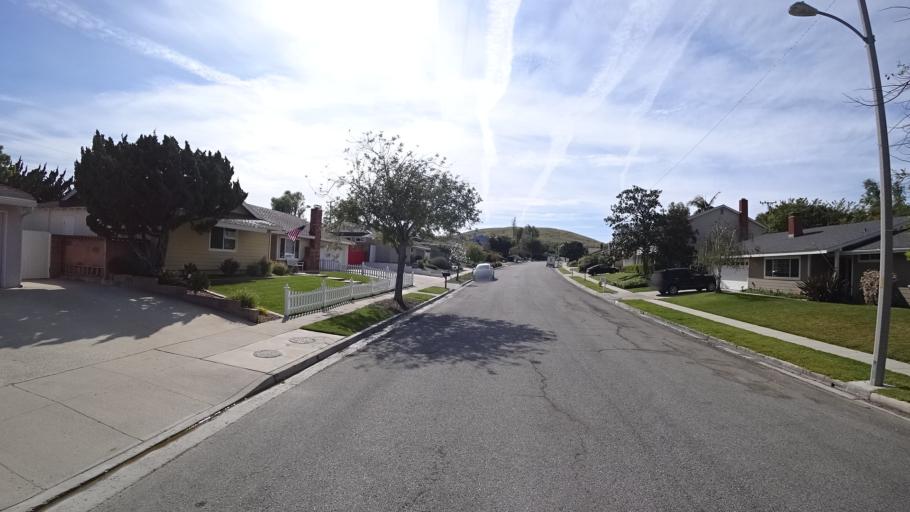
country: US
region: California
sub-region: Ventura County
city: Thousand Oaks
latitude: 34.2055
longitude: -118.8766
